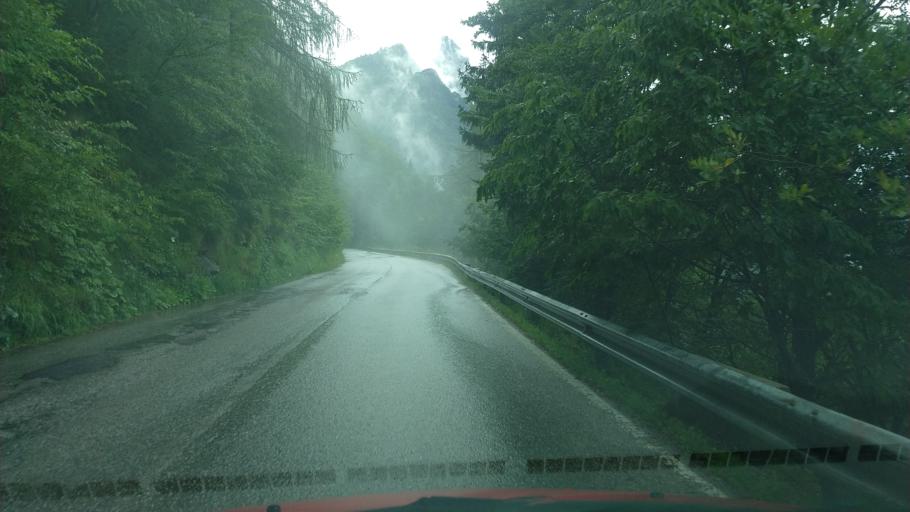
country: IT
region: Veneto
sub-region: Provincia di Vicenza
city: Tonezza del Cimone
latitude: 45.8701
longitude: 11.3361
